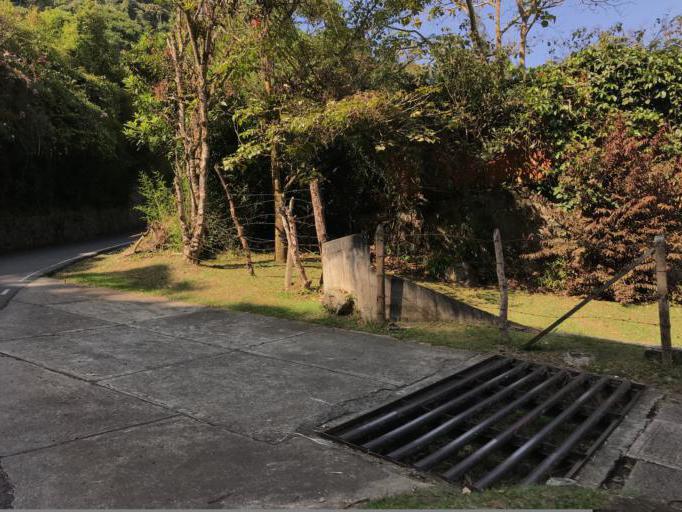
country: CO
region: Valle del Cauca
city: Cali
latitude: 3.4749
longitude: -76.6176
